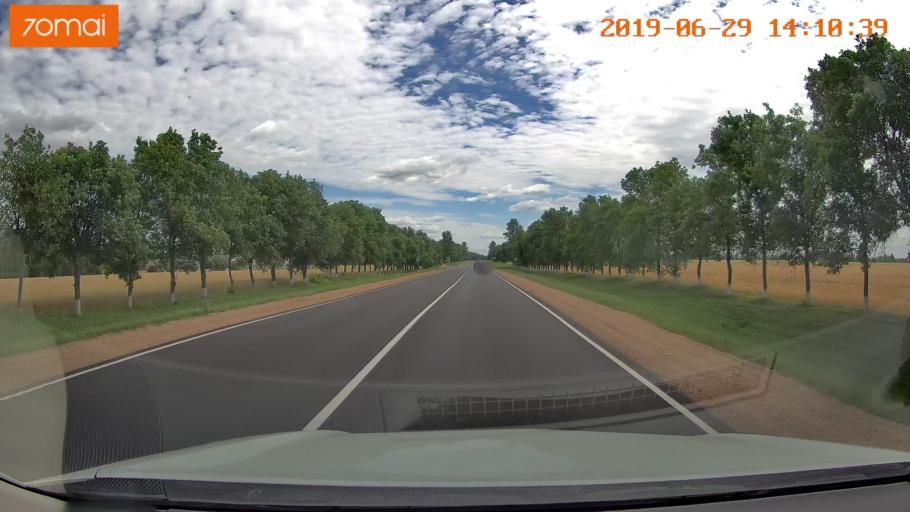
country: BY
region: Minsk
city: Salihorsk
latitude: 52.8255
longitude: 27.4979
